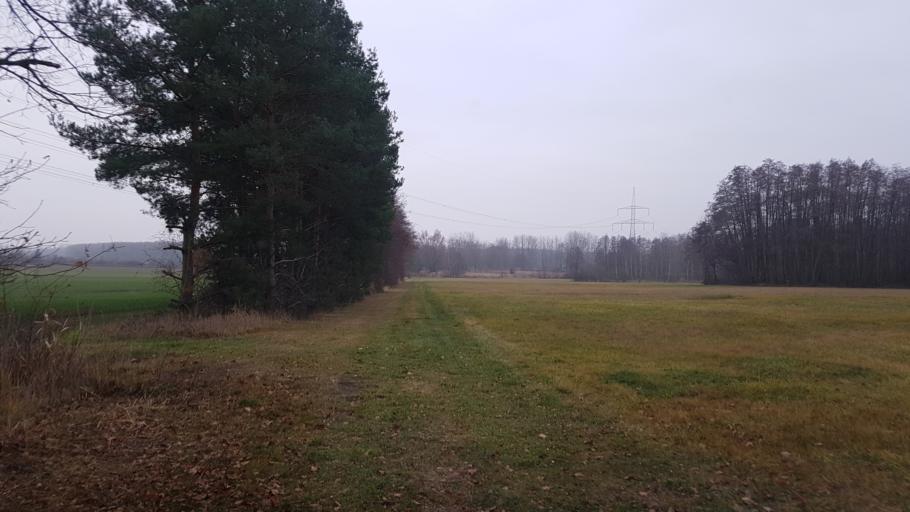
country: DE
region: Brandenburg
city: Doberlug-Kirchhain
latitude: 51.6305
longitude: 13.5345
